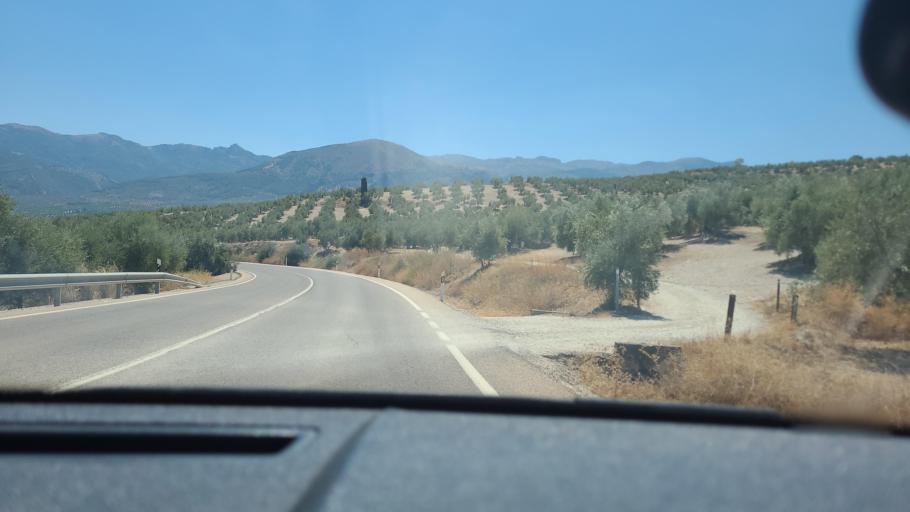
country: ES
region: Andalusia
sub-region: Provincia de Jaen
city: Jimena
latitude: 37.8317
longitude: -3.4460
